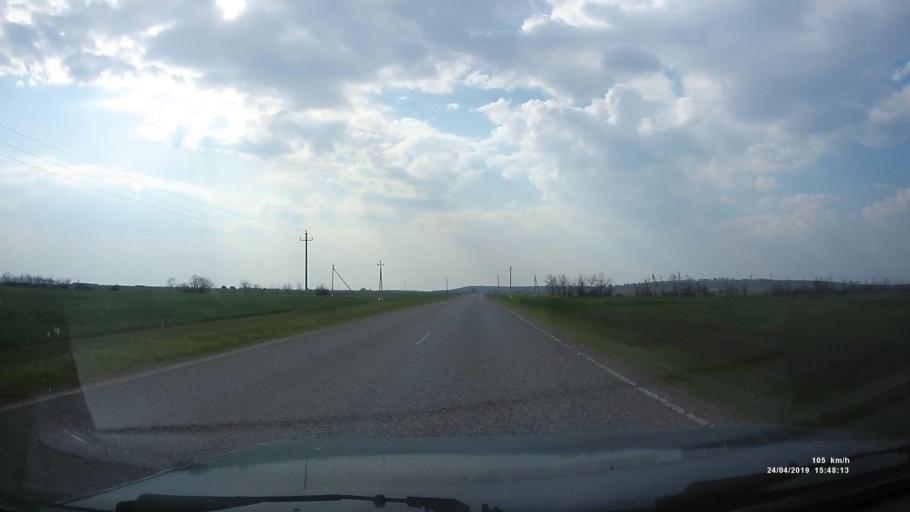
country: RU
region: Kalmykiya
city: Yashalta
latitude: 46.5974
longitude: 42.6805
